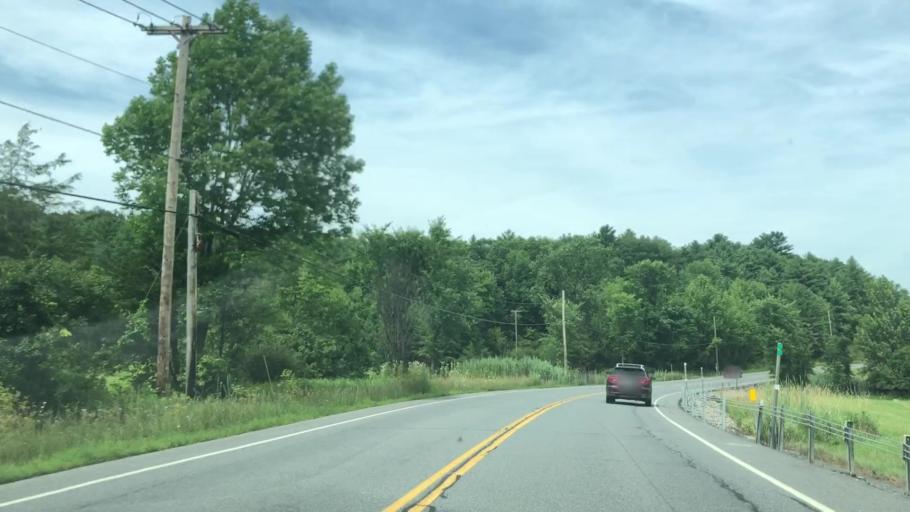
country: US
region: New York
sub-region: Washington County
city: Whitehall
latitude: 43.4933
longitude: -73.4288
